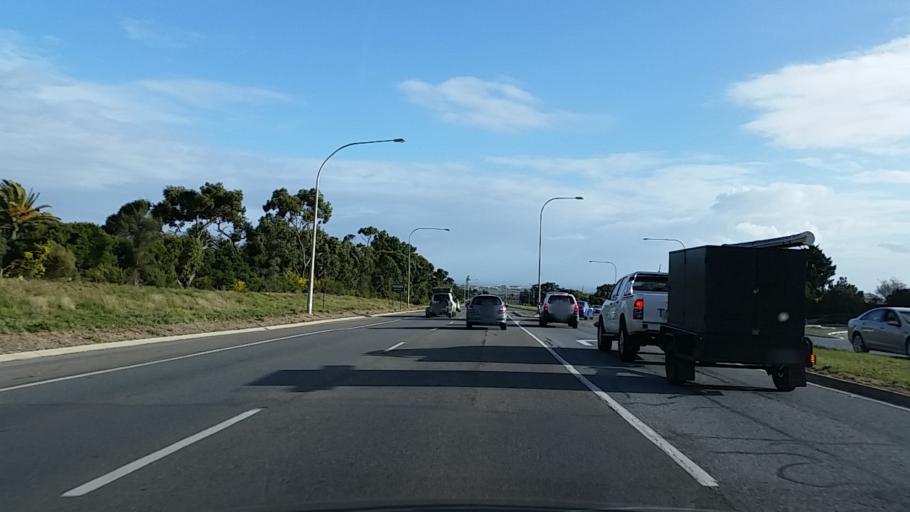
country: AU
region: South Australia
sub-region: Marion
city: Happy Valley
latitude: -35.0693
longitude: 138.5284
